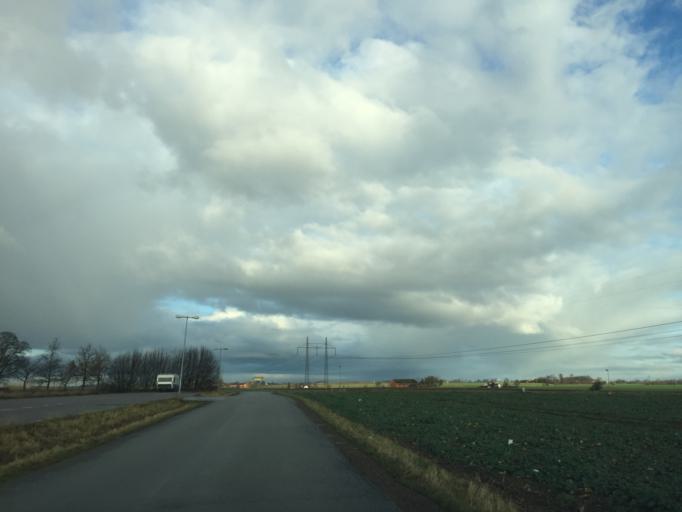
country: SE
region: Skane
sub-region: Lomma Kommun
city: Lomma
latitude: 55.7241
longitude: 13.0936
